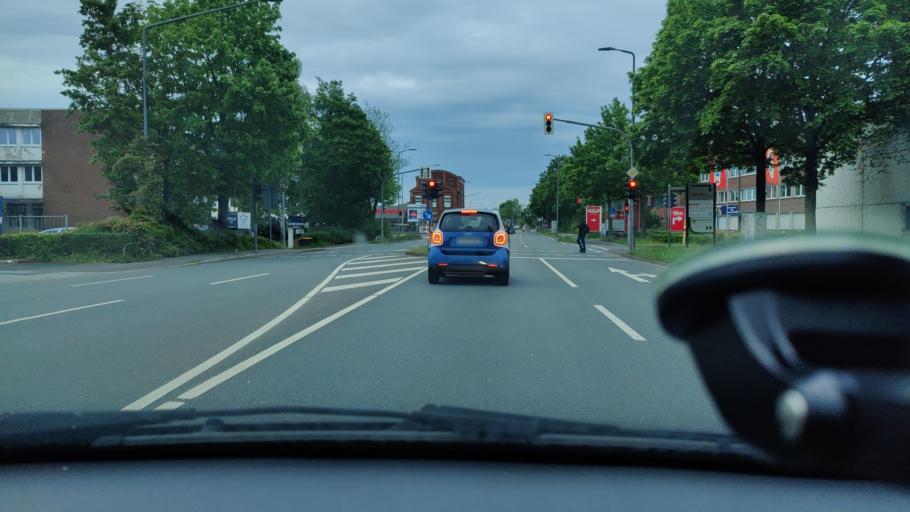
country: DE
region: North Rhine-Westphalia
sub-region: Regierungsbezirk Dusseldorf
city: Ratingen
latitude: 51.2982
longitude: 6.8307
